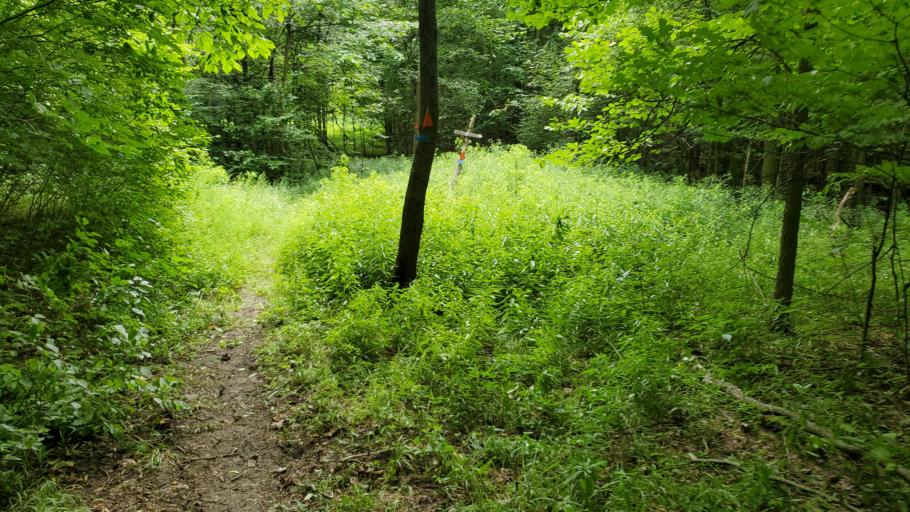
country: CA
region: Ontario
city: Gananoque
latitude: 44.5516
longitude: -76.3695
